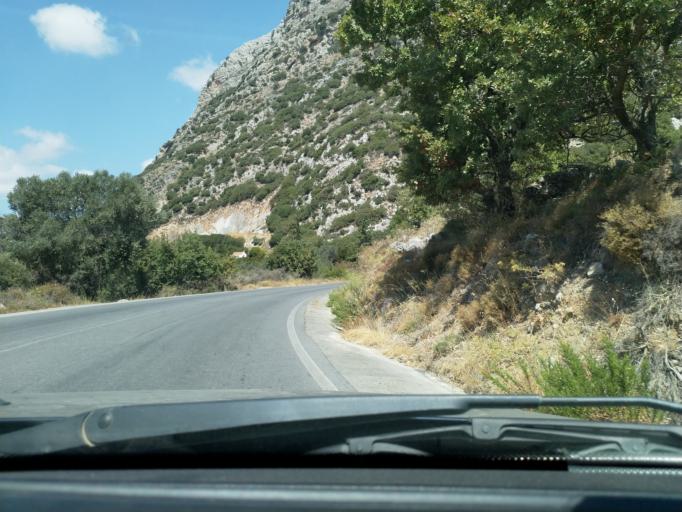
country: GR
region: Crete
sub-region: Nomos Rethymnis
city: Agia Foteini
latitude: 35.2030
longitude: 24.5431
